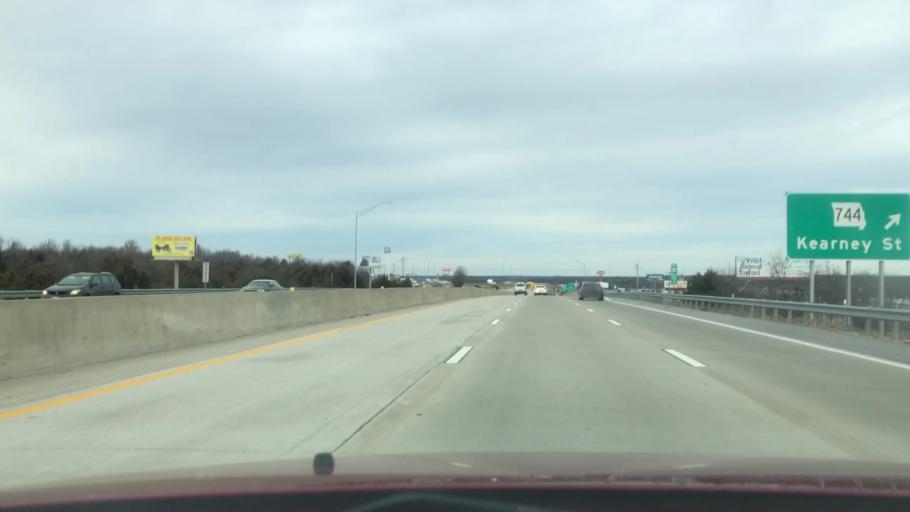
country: US
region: Missouri
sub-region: Greene County
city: Springfield
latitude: 37.2341
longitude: -93.2249
